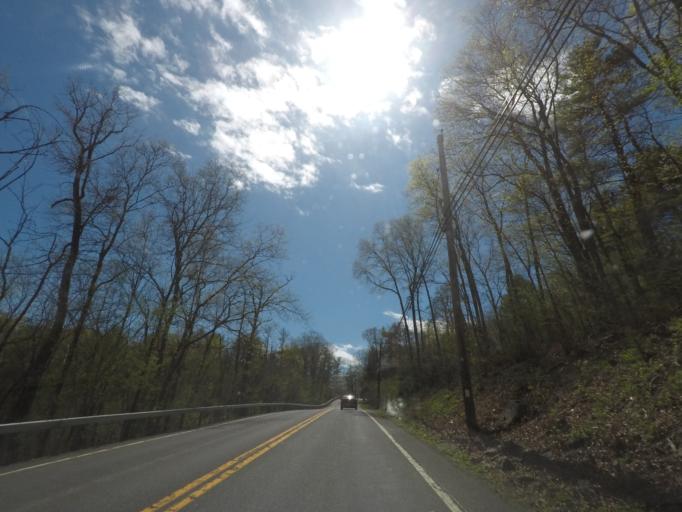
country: US
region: New York
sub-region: Greene County
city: Athens
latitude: 42.2479
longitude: -73.8416
